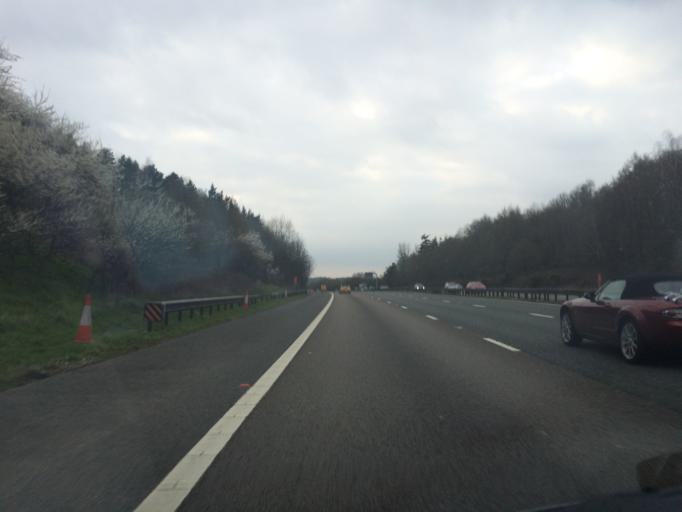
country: GB
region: England
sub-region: West Berkshire
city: Hermitage
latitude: 51.4610
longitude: -1.2093
